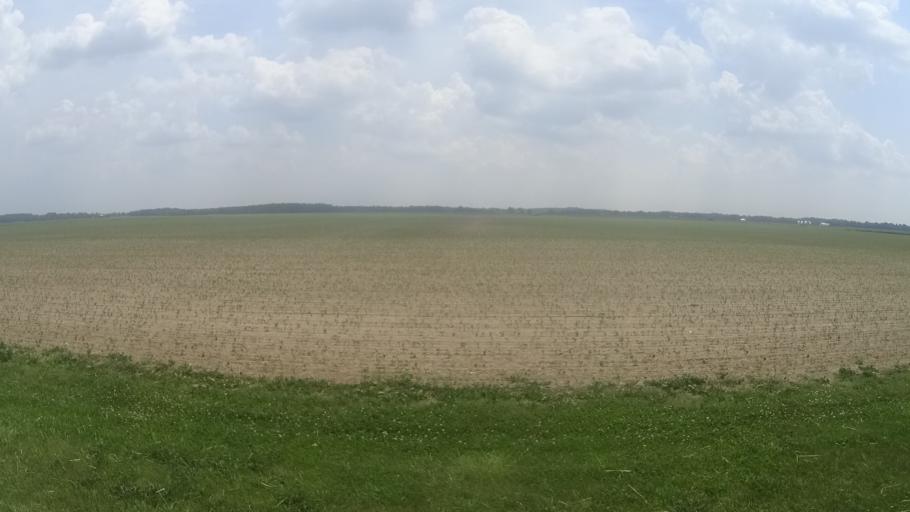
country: US
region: Ohio
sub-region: Huron County
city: Monroeville
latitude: 41.2976
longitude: -82.6924
